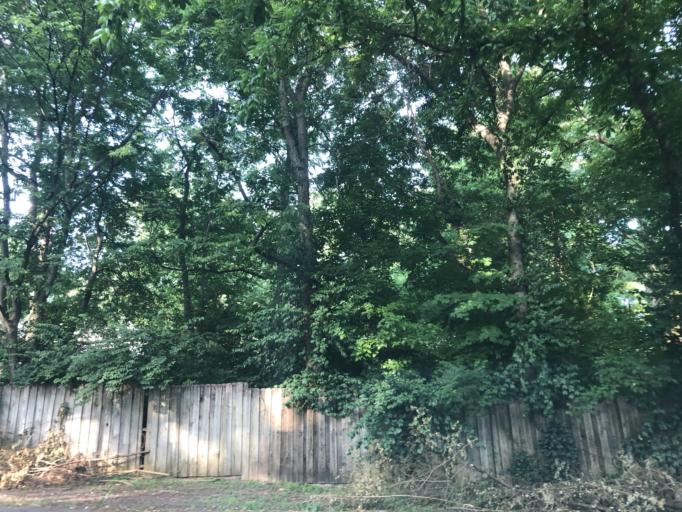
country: US
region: Tennessee
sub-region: Davidson County
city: Oak Hill
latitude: 36.1180
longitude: -86.7843
